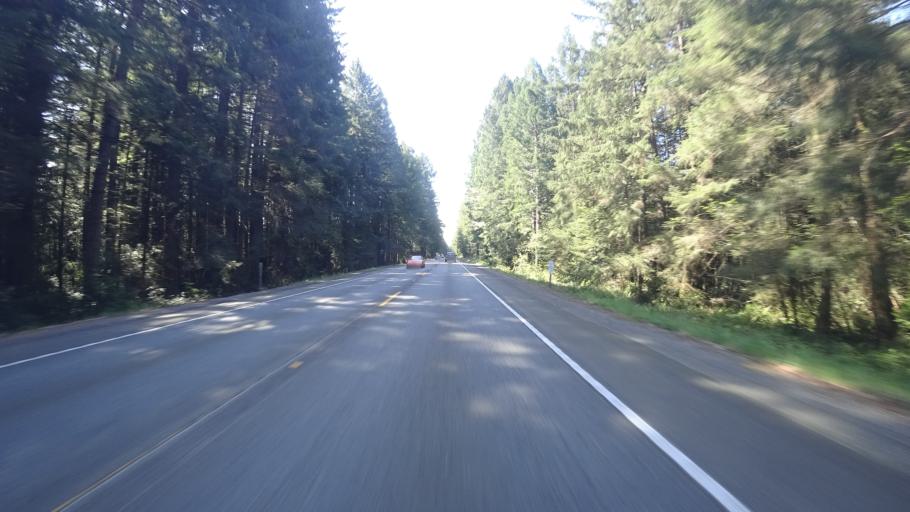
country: US
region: California
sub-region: Del Norte County
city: Bertsch-Oceanview
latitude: 41.8346
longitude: -124.1442
